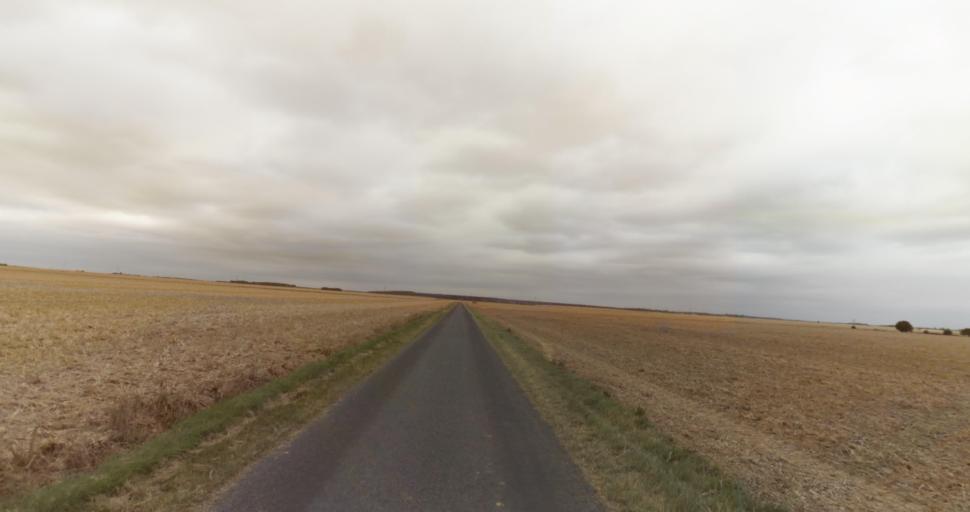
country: FR
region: Haute-Normandie
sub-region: Departement de l'Eure
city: La Couture-Boussey
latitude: 48.9333
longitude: 1.3287
